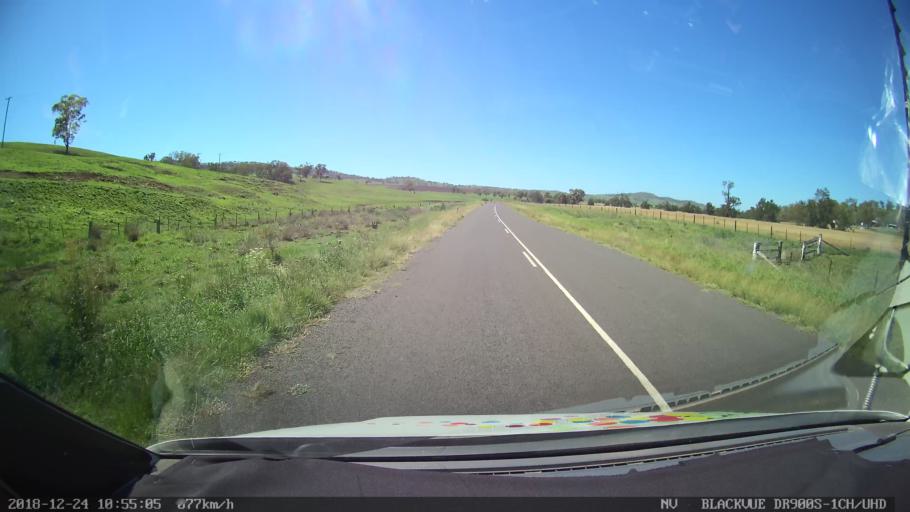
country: AU
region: New South Wales
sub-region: Upper Hunter Shire
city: Merriwa
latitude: -32.0119
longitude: 150.4180
